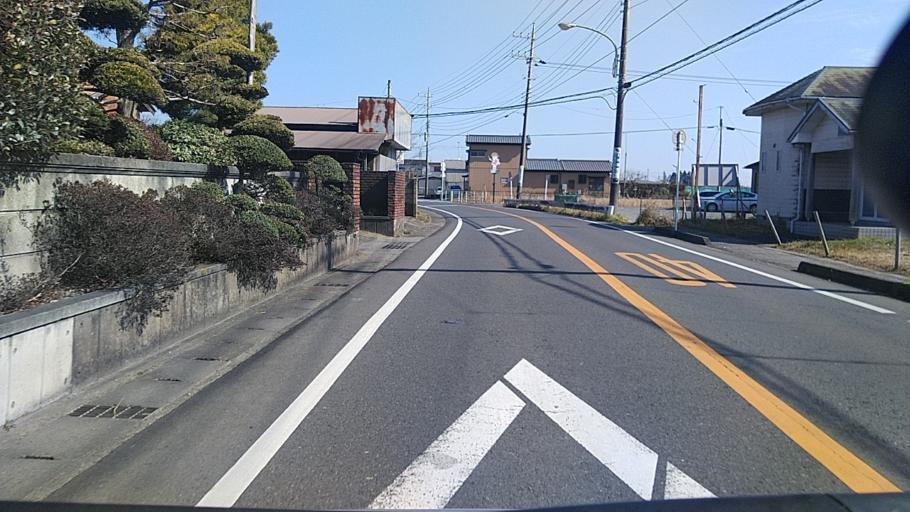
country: JP
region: Chiba
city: Mobara
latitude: 35.4241
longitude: 140.2708
